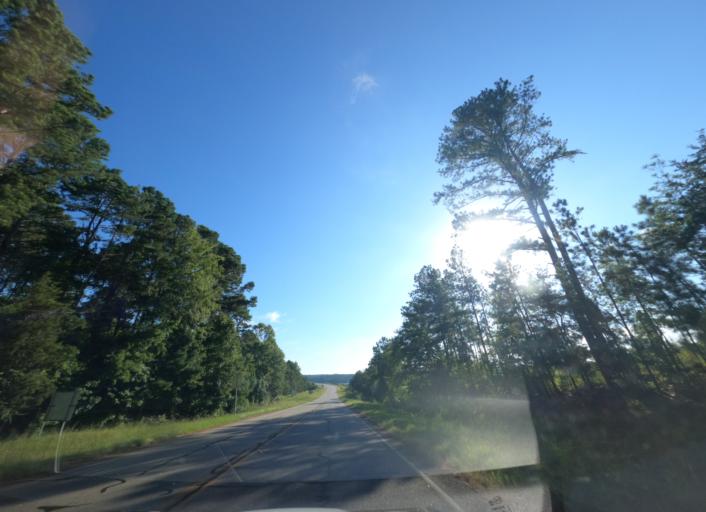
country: US
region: Georgia
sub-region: Lincoln County
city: Lincolnton
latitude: 33.8519
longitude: -82.3945
